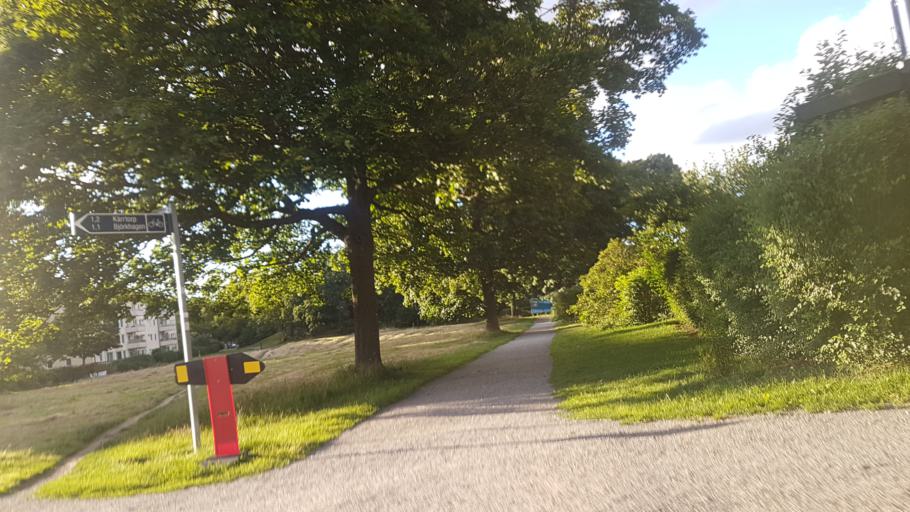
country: SE
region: Stockholm
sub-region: Stockholms Kommun
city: OEstermalm
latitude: 59.2911
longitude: 18.1092
